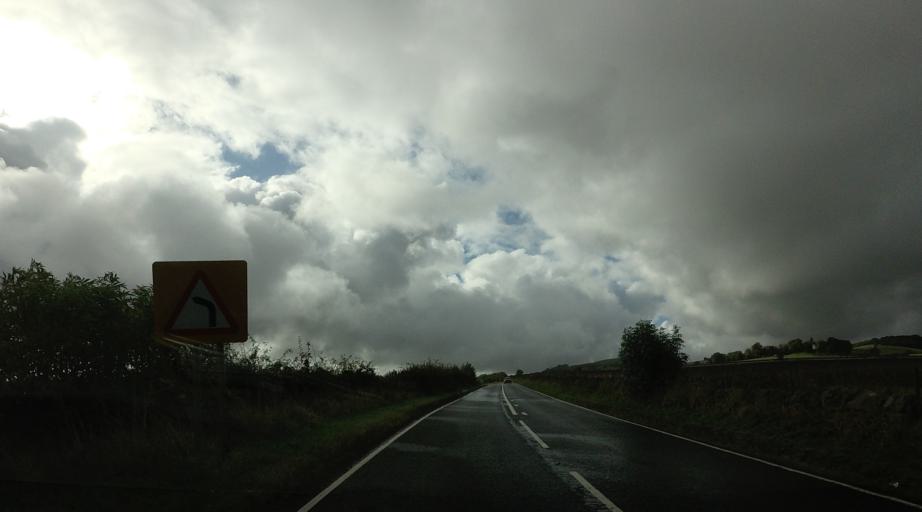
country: GB
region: Scotland
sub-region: Fife
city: Balmullo
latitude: 56.3636
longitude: -2.9372
